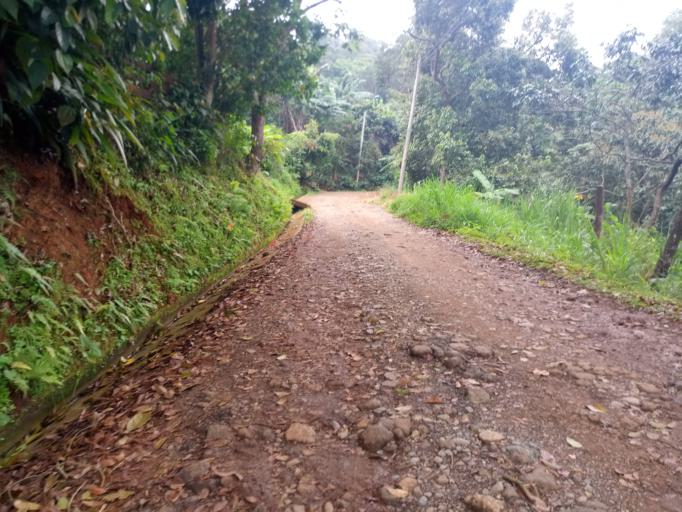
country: CO
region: Valle del Cauca
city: Cali
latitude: 3.5070
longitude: -76.5645
